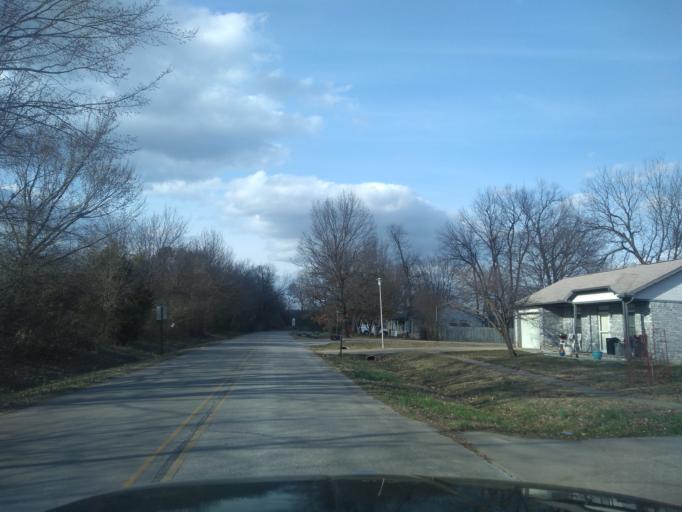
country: US
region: Arkansas
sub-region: Washington County
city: Farmington
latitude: 36.0487
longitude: -94.2405
